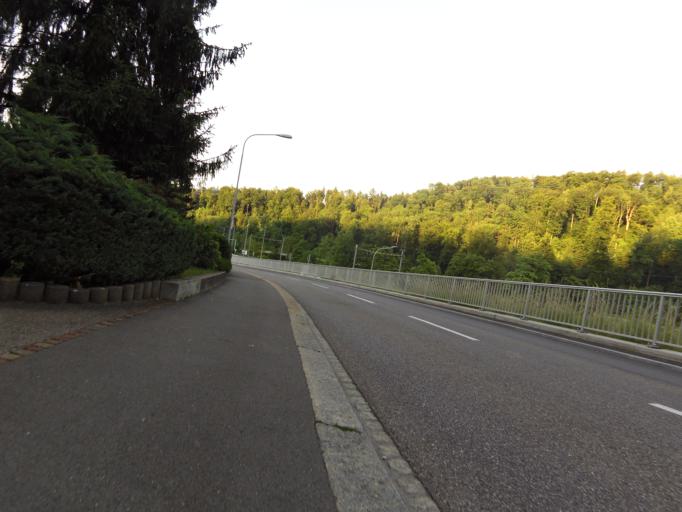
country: CH
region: Zurich
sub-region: Bezirk Zuerich
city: Zuerich (Kreis 2) / Unter-Leimbach
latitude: 47.3320
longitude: 8.5169
